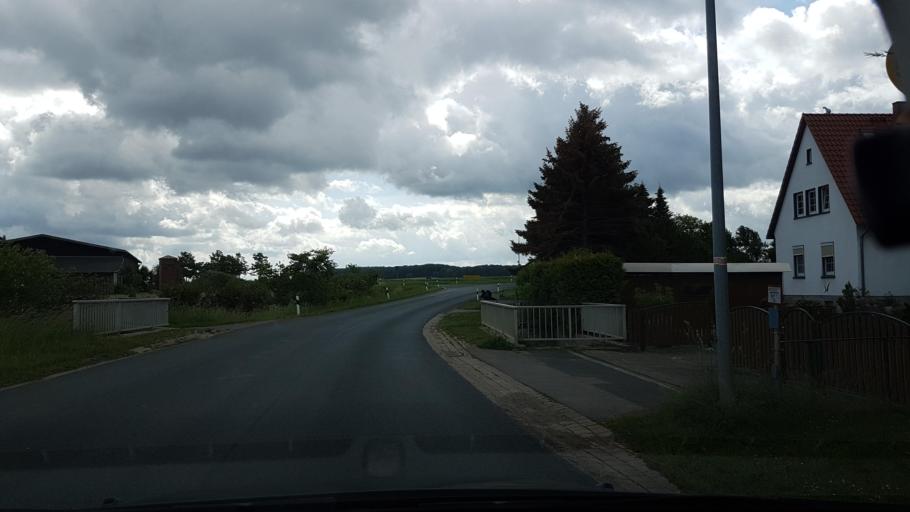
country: DE
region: Lower Saxony
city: Elze
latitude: 52.1431
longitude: 9.6670
